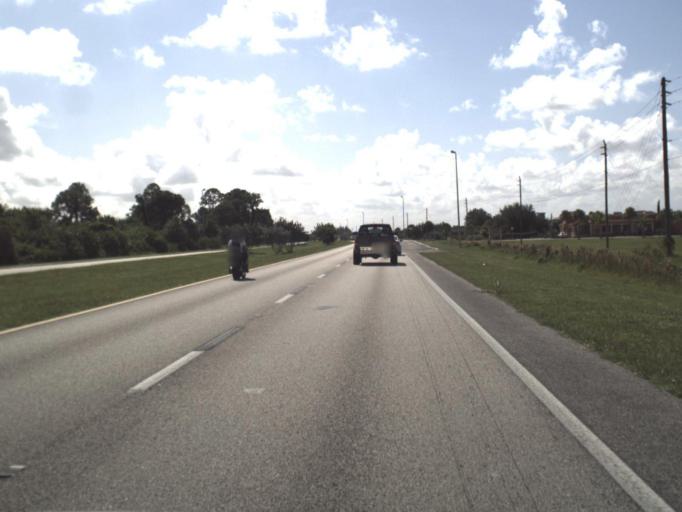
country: US
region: Florida
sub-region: Charlotte County
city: Charlotte Park
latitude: 26.8807
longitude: -82.0136
